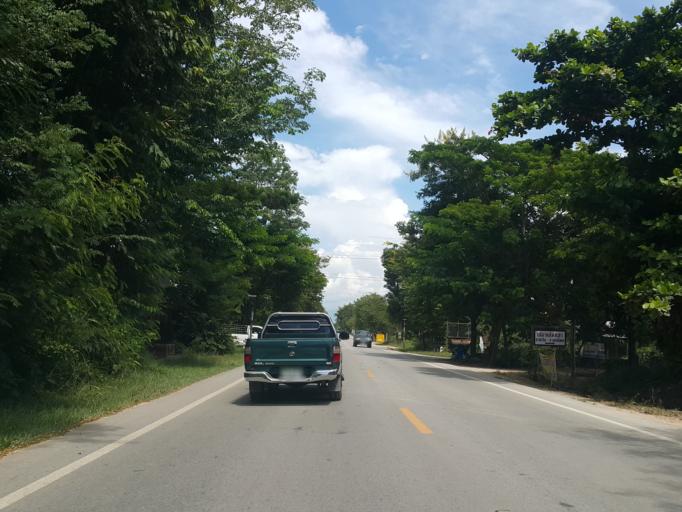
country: TH
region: Chiang Mai
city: Phrao
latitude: 19.3060
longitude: 99.1895
